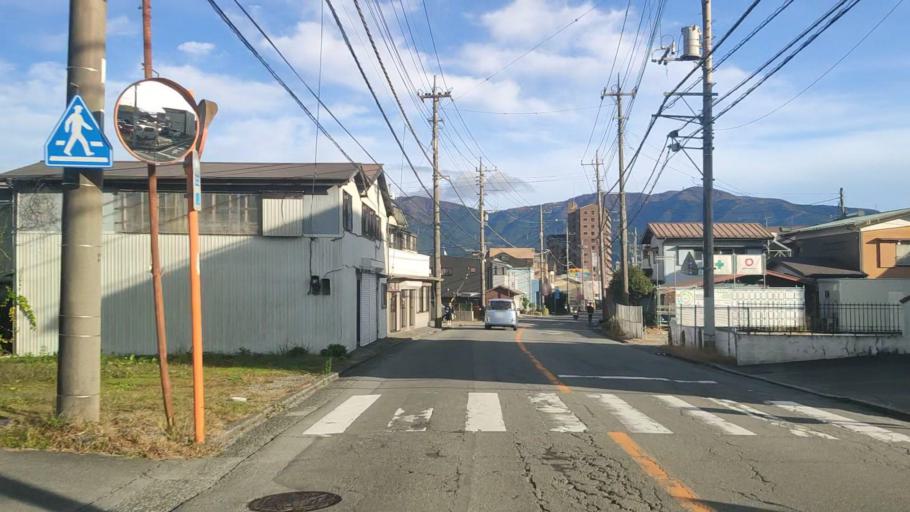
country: JP
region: Shizuoka
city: Gotemba
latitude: 35.3034
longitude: 138.9272
